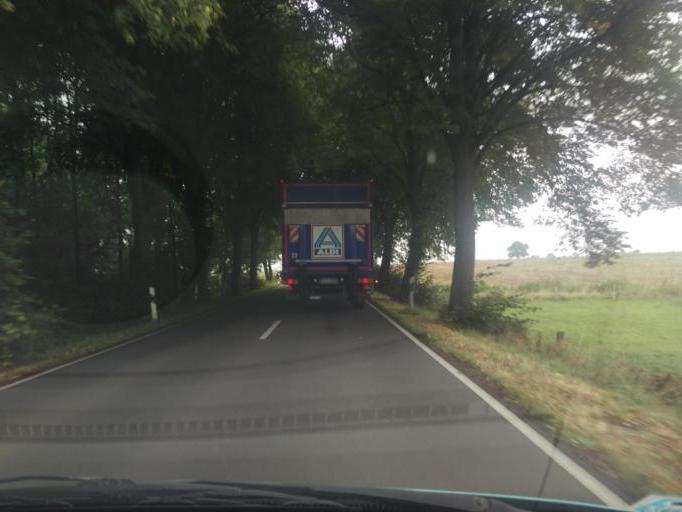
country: DE
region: Lower Saxony
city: Dollbergen
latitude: 52.4357
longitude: 10.1879
